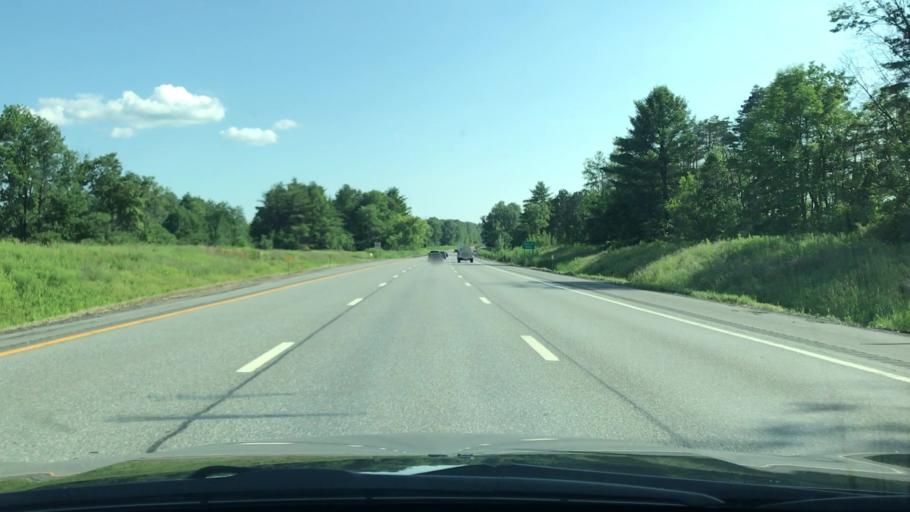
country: US
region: New York
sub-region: Warren County
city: West Glens Falls
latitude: 43.2060
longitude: -73.6958
